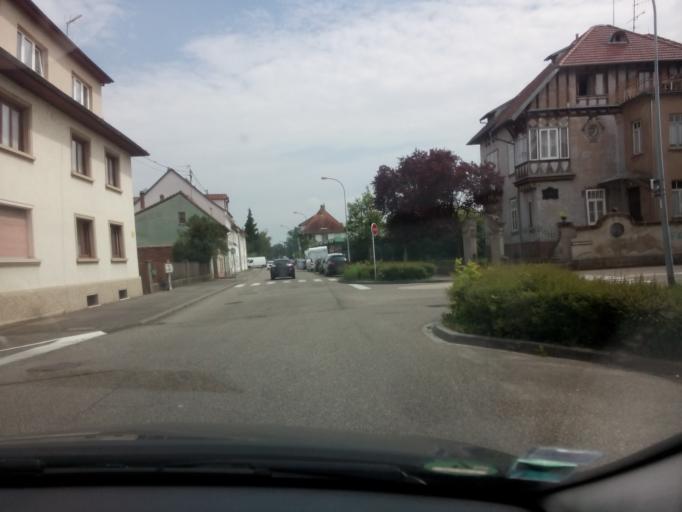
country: FR
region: Alsace
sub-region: Departement du Bas-Rhin
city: Bischwiller
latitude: 48.7662
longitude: 7.8650
